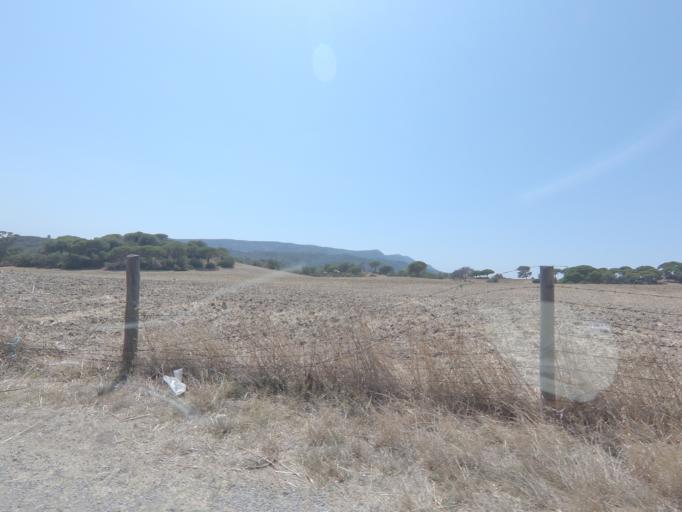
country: PT
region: Setubal
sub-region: Palmela
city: Quinta do Anjo
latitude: 38.5254
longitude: -8.9335
